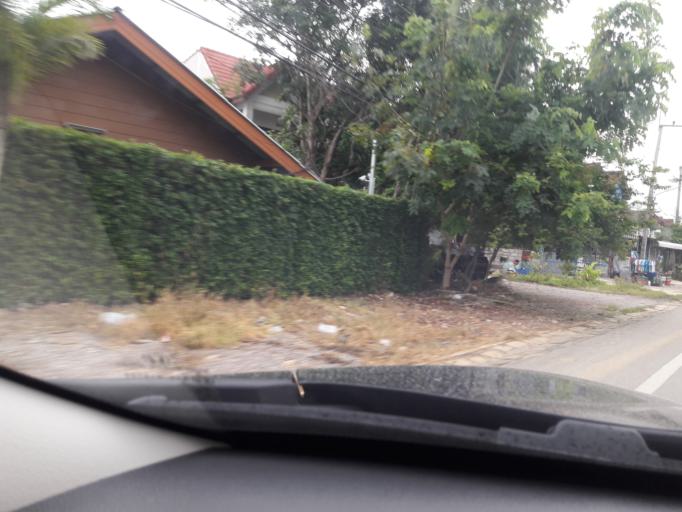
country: TH
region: Ratchaburi
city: Damnoen Saduak
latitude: 13.5280
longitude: 99.9608
